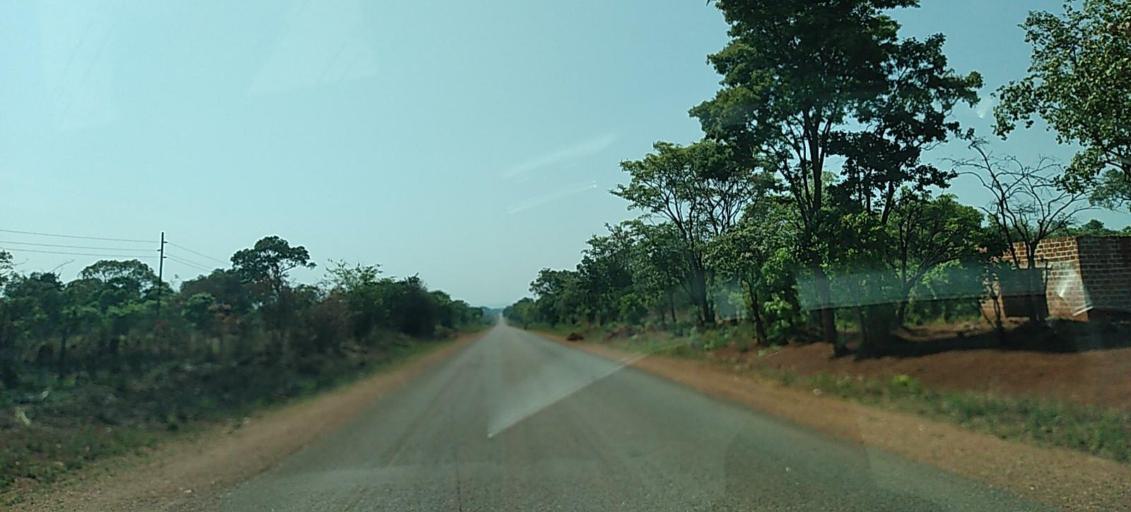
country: ZM
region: North-Western
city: Solwezi
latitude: -12.1193
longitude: 25.5115
